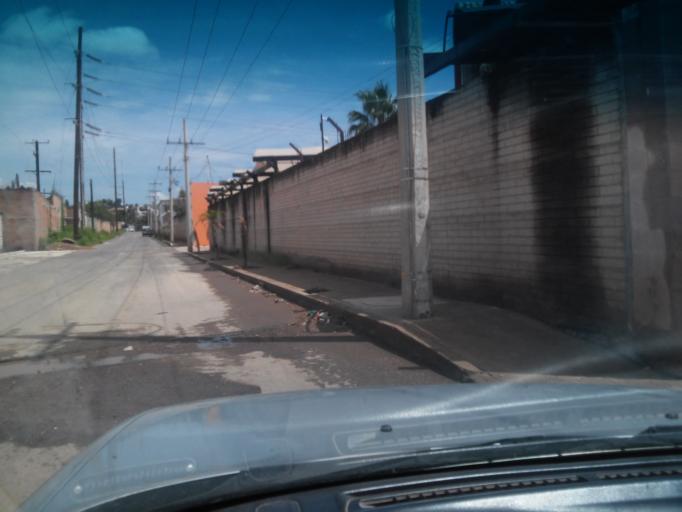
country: MX
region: Durango
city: Victoria de Durango
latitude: 24.0071
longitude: -104.6972
